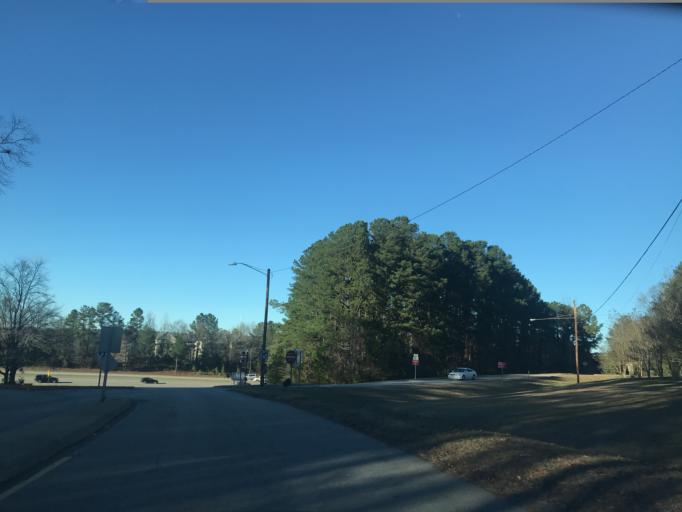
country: US
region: North Carolina
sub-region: Wake County
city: West Raleigh
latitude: 35.8318
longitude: -78.6741
